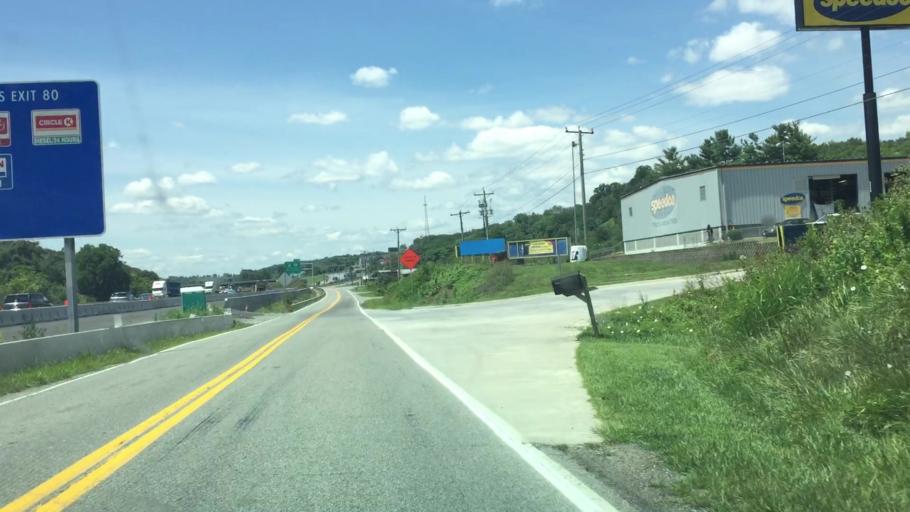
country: US
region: Virginia
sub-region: Wythe County
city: Wytheville
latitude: 36.9468
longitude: -80.9415
